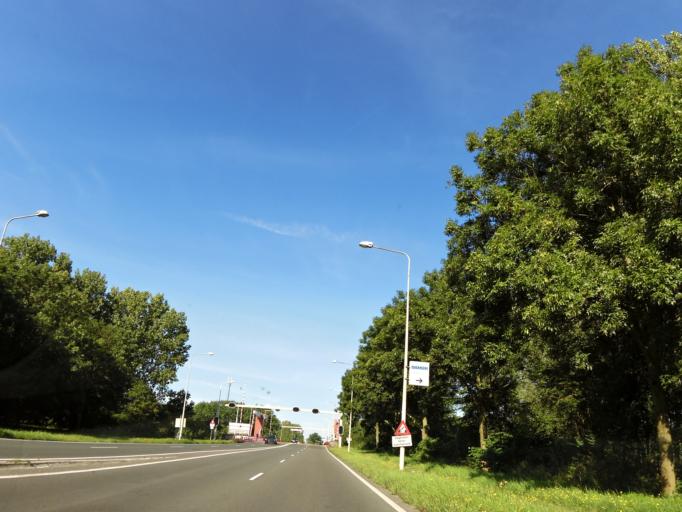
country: NL
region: Zeeland
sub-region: Gemeente Vlissingen
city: Vlissingen
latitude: 51.4575
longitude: 3.5927
